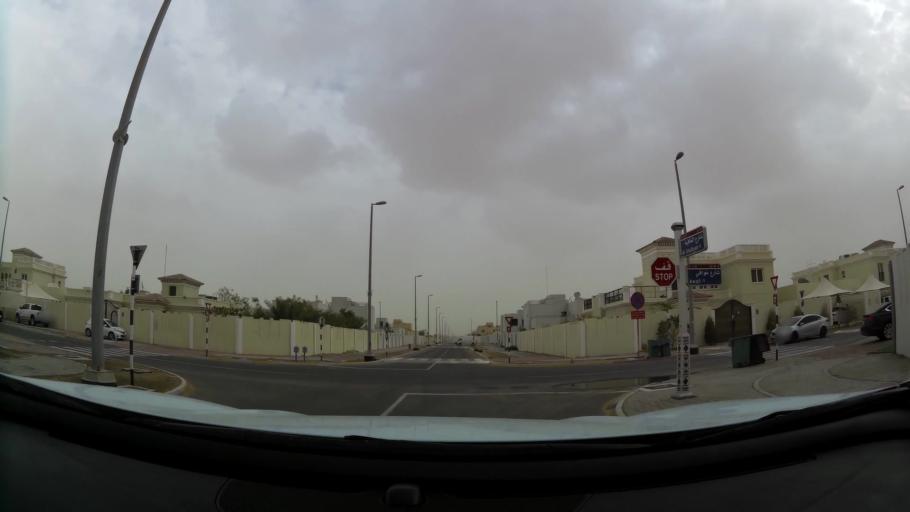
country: AE
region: Abu Dhabi
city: Abu Dhabi
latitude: 24.4490
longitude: 54.7148
